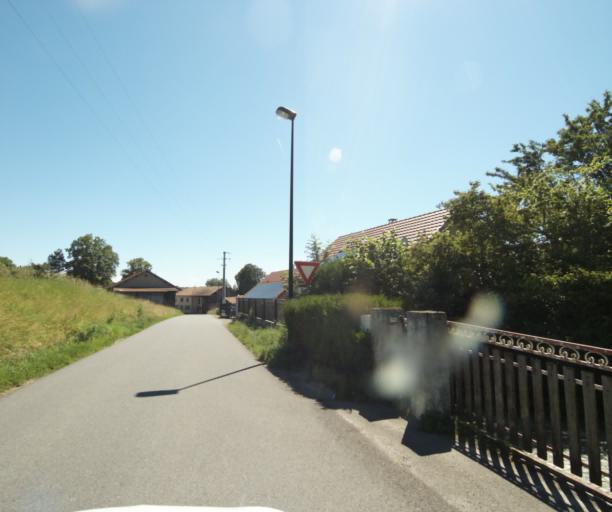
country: FR
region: Rhone-Alpes
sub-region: Departement de la Haute-Savoie
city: Loisin
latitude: 46.2736
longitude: 6.3137
